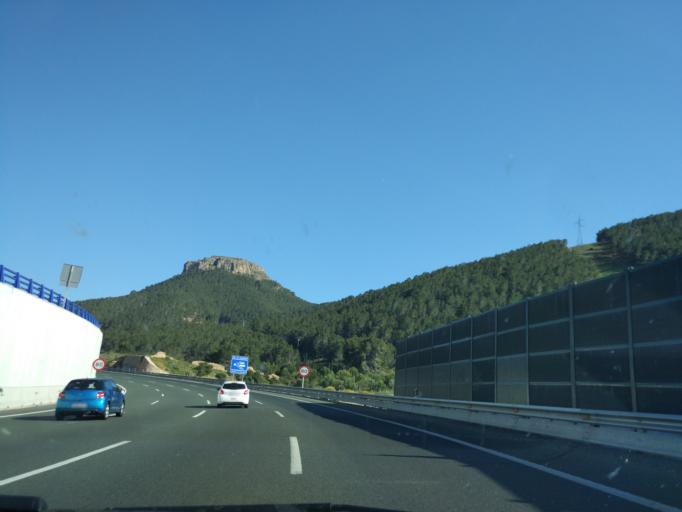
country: ES
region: Murcia
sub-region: Murcia
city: Alcantarilla
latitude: 37.9096
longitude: -1.1631
